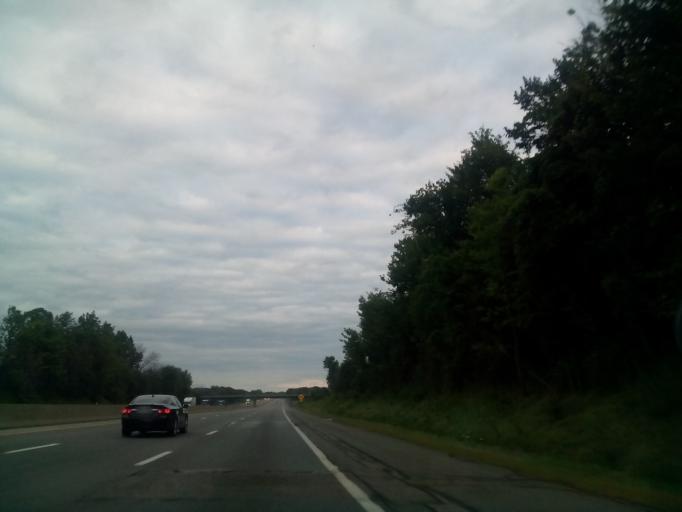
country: US
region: Ohio
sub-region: Portage County
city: Garrettsville
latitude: 41.2432
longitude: -81.1526
